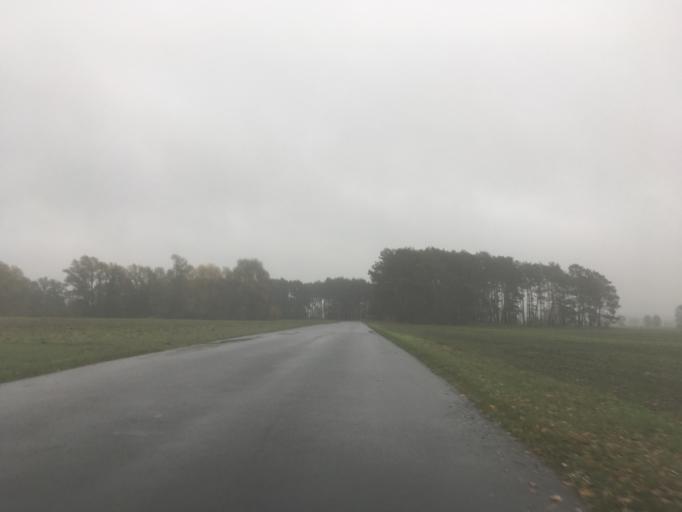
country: DE
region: Brandenburg
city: Schlepzig
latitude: 52.0151
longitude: 13.9472
